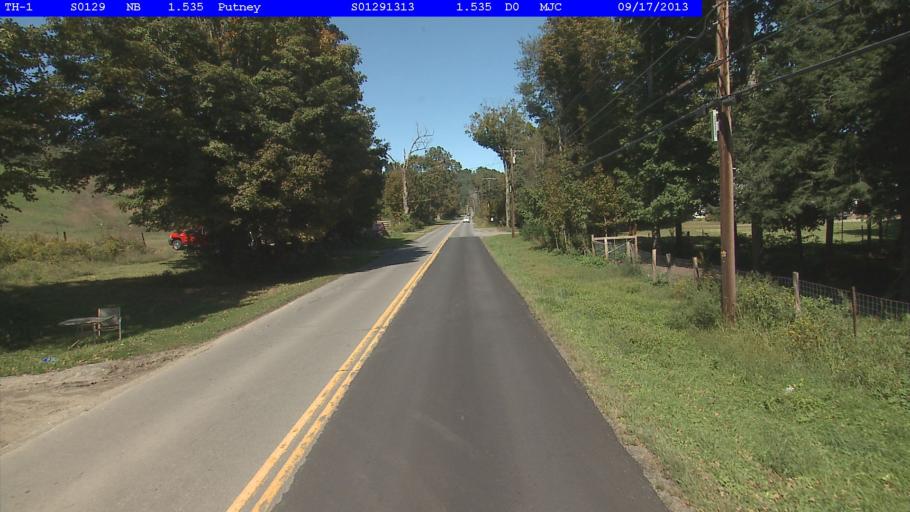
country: US
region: New Hampshire
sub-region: Cheshire County
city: Westmoreland
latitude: 42.9947
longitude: -72.5320
